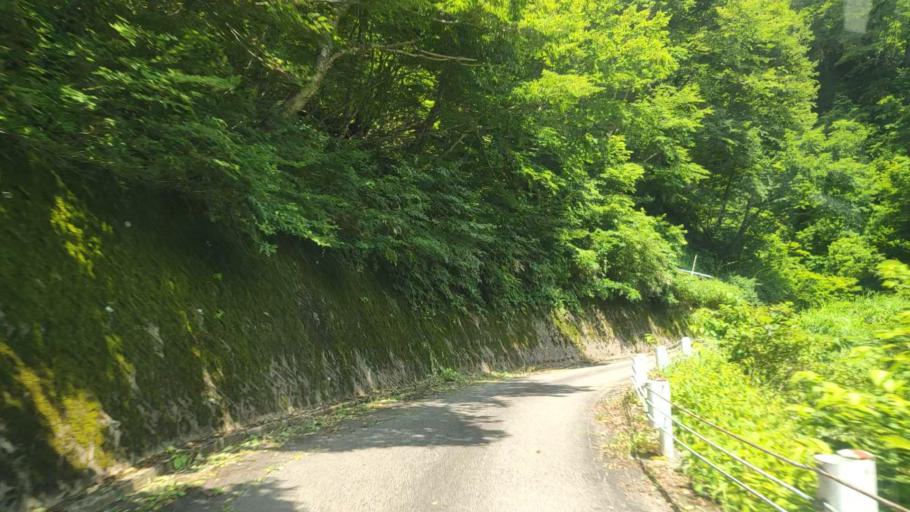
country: JP
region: Fukui
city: Ono
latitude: 35.7906
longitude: 136.5035
